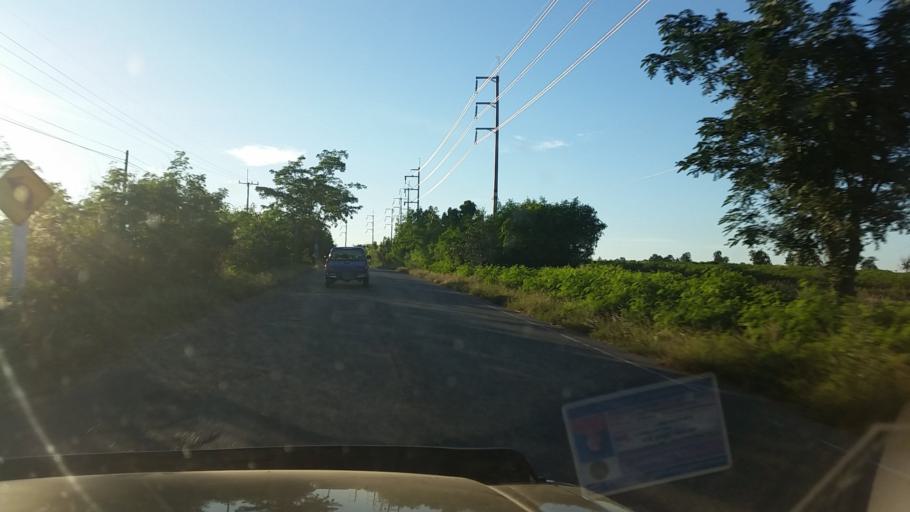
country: TH
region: Chaiyaphum
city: Nong Bua Rawe
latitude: 15.6909
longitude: 101.7099
